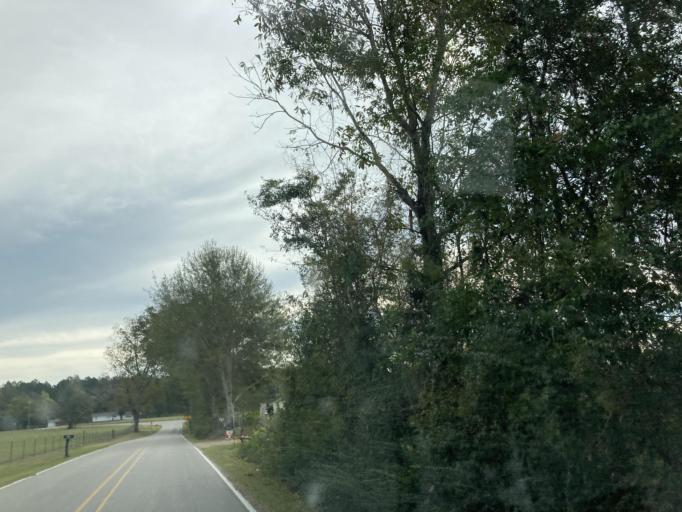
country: US
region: Mississippi
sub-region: Lamar County
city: Purvis
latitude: 31.1114
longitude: -89.4752
